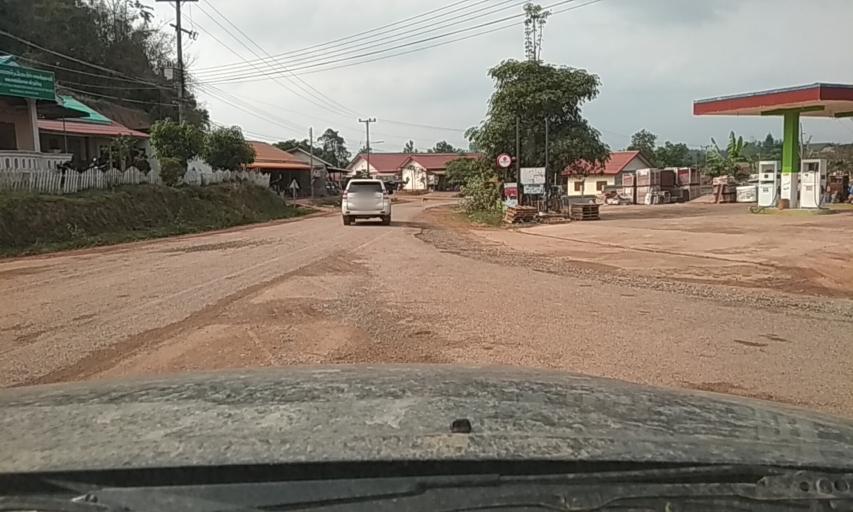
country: TH
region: Nan
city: Mae Charim
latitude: 18.3995
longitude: 101.1774
